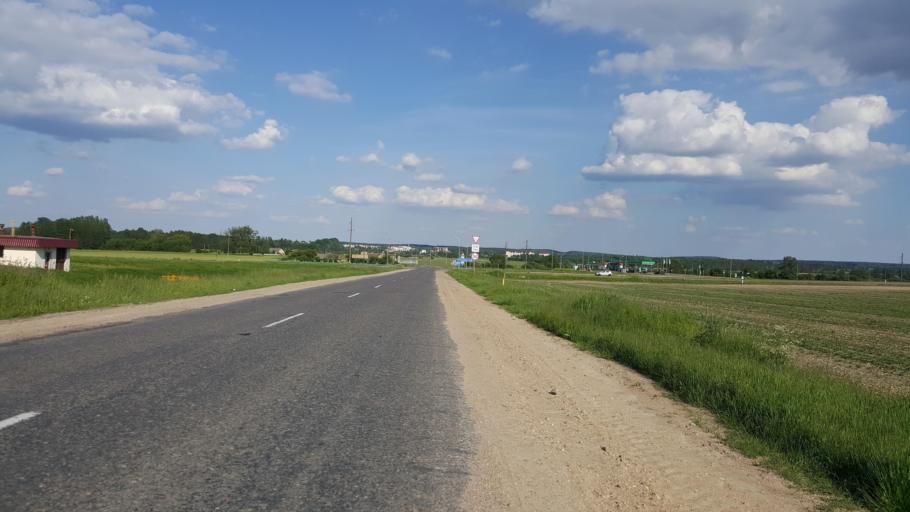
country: BY
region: Brest
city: Kamyanyets
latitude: 52.3996
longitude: 23.7813
